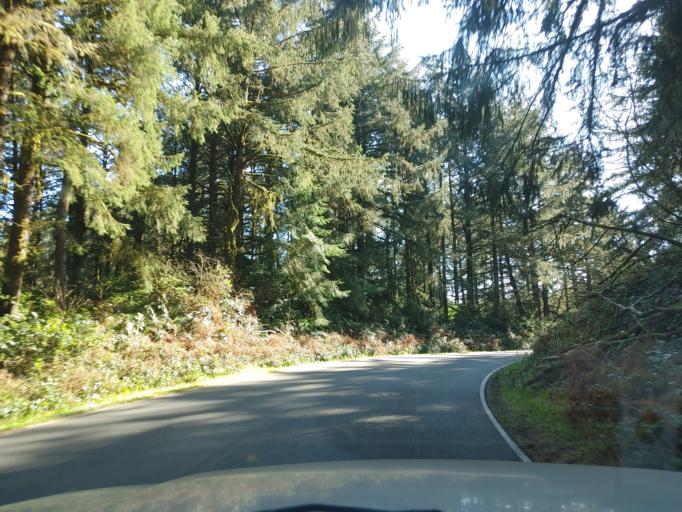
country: US
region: Oregon
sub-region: Clatsop County
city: Warrenton
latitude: 46.1800
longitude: -123.9647
